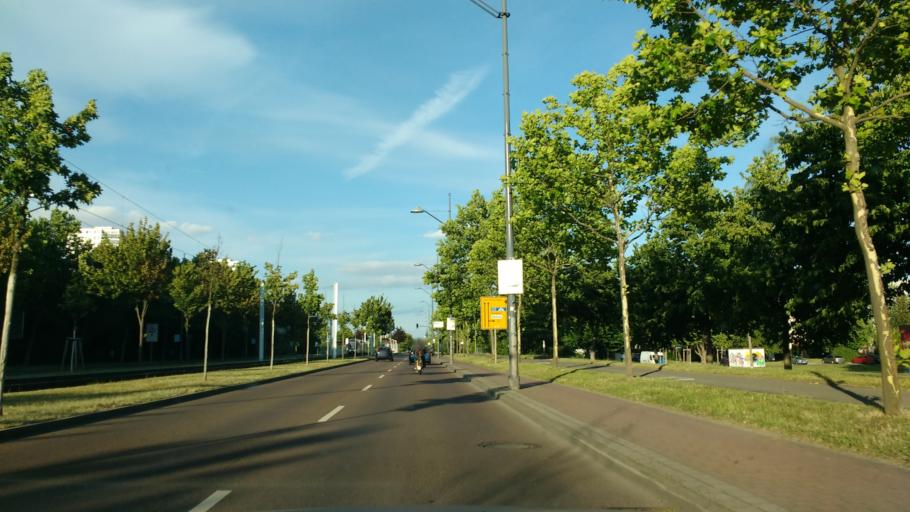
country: DE
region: Saxony-Anhalt
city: Halle Neustadt
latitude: 51.4810
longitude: 11.9376
